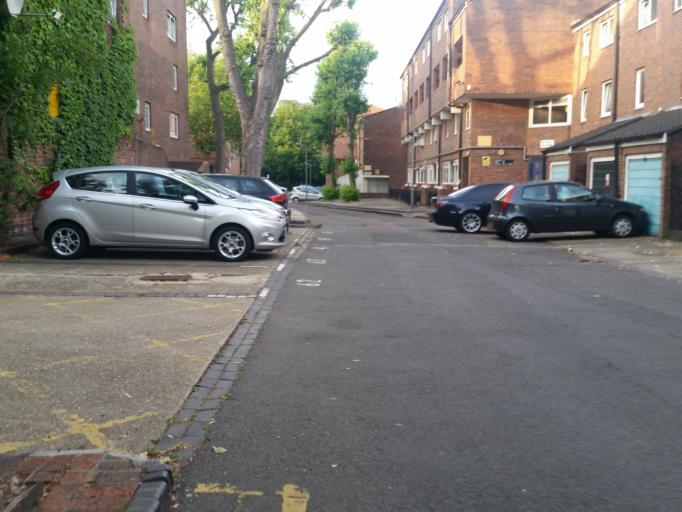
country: GB
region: England
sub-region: Greater London
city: Crouch End
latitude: 51.5693
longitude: -0.1280
